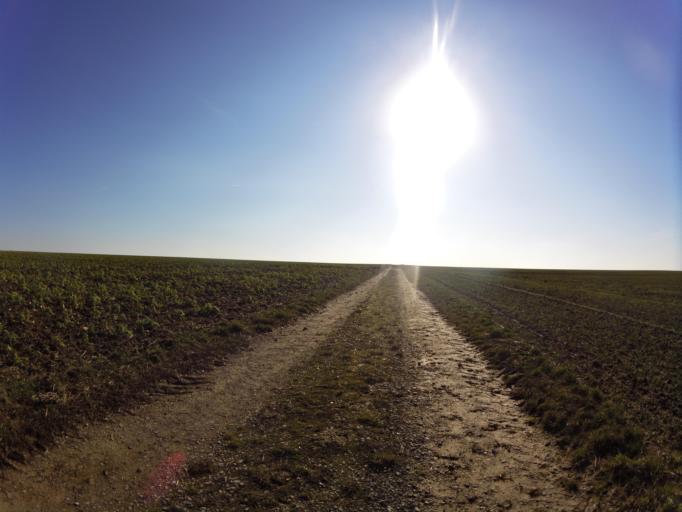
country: DE
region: Bavaria
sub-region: Regierungsbezirk Unterfranken
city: Giebelstadt
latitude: 49.6872
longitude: 9.9702
